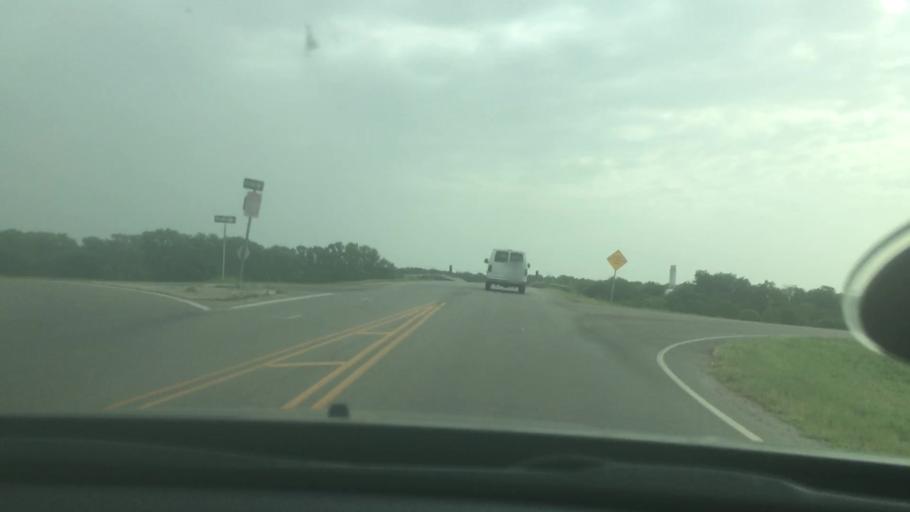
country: US
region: Oklahoma
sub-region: Pontotoc County
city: Ada
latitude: 34.7374
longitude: -96.6462
